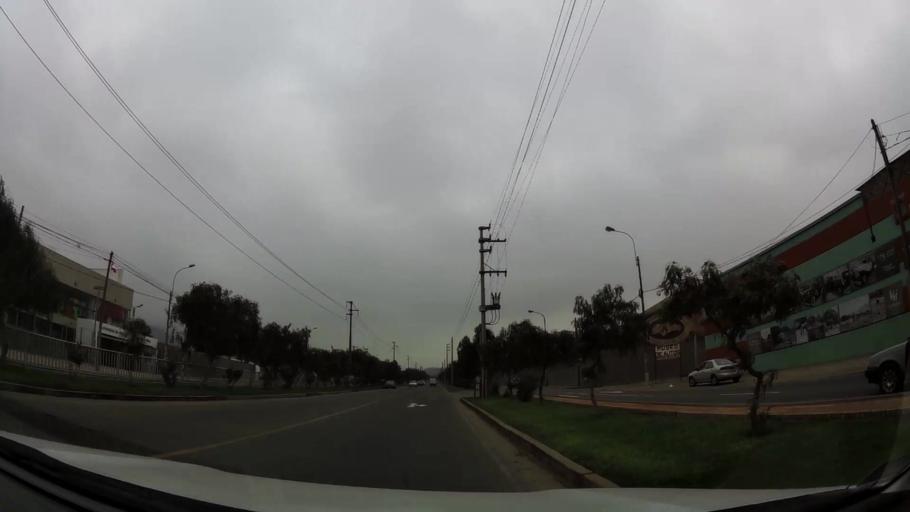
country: PE
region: Lima
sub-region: Lima
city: La Molina
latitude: -12.0862
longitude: -76.9088
